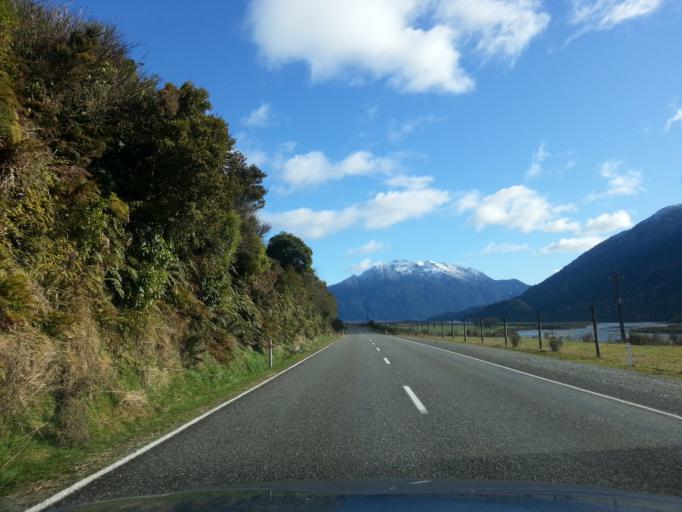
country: NZ
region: West Coast
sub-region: Grey District
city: Greymouth
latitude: -42.7361
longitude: 171.4362
